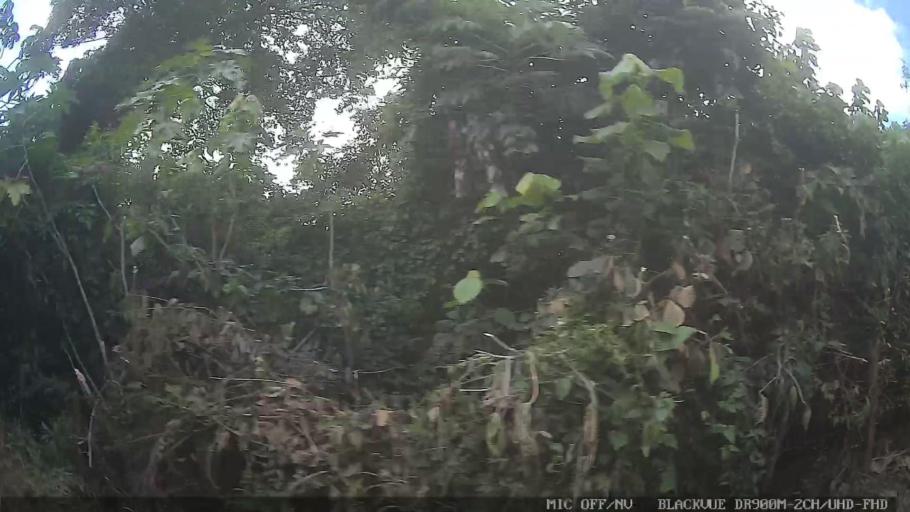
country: BR
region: Sao Paulo
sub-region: Braganca Paulista
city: Braganca Paulista
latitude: -22.9170
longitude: -46.4465
